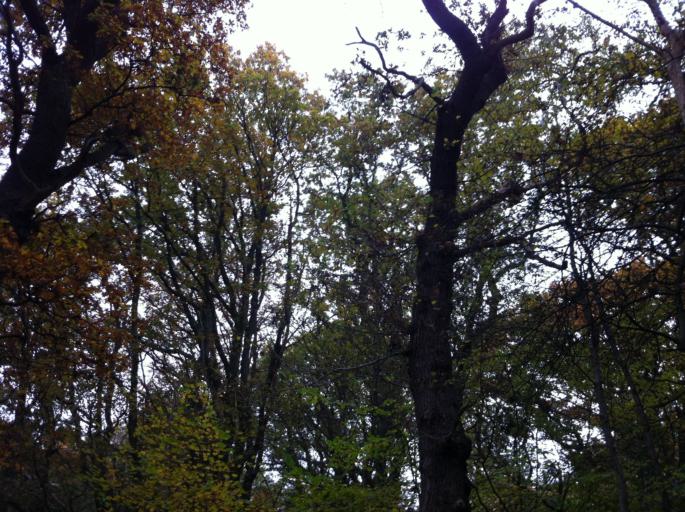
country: SE
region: Skane
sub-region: Helsingborg
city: Gantofta
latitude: 55.9958
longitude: 12.7977
